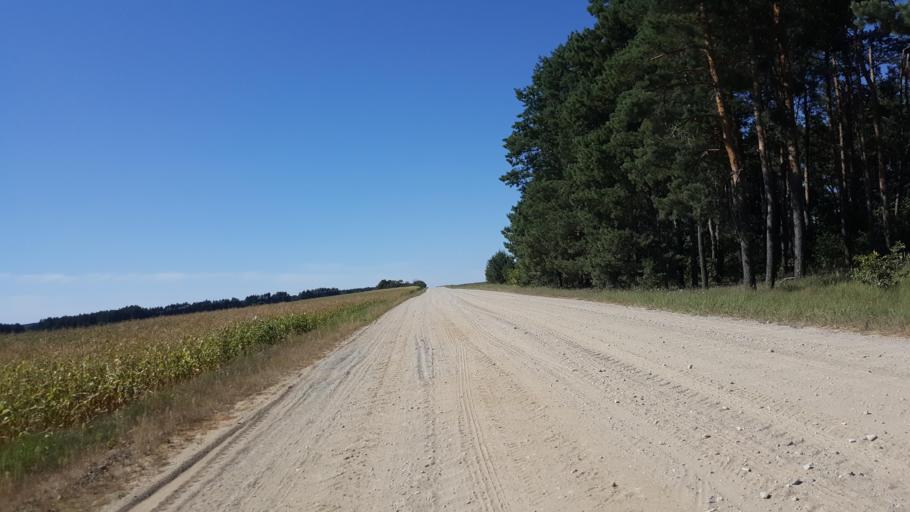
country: PL
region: Lublin Voivodeship
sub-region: Powiat bialski
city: Rokitno
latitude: 52.2265
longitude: 23.3340
